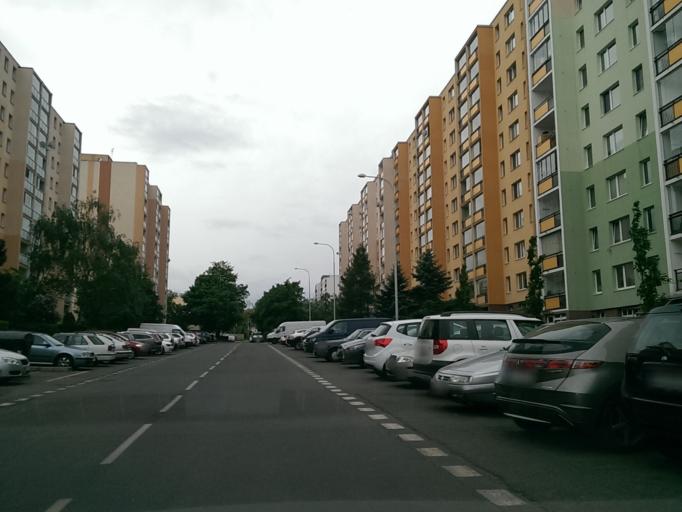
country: CZ
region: Central Bohemia
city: Vestec
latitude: 50.0383
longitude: 14.5044
